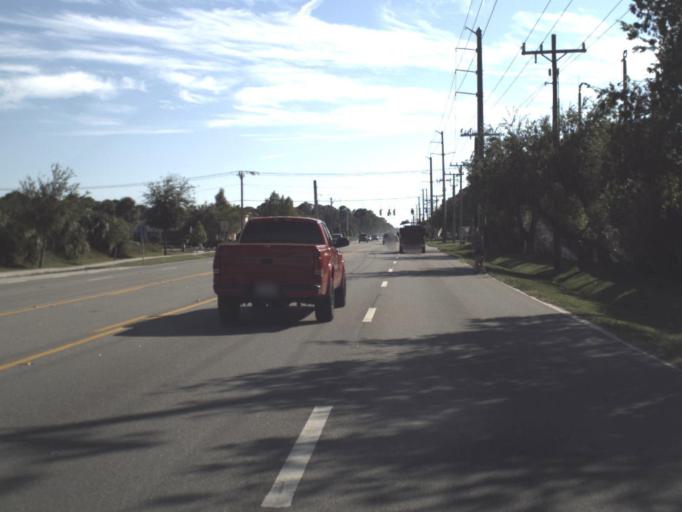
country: US
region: Florida
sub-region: Brevard County
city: June Park
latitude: 28.1151
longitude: -80.6727
